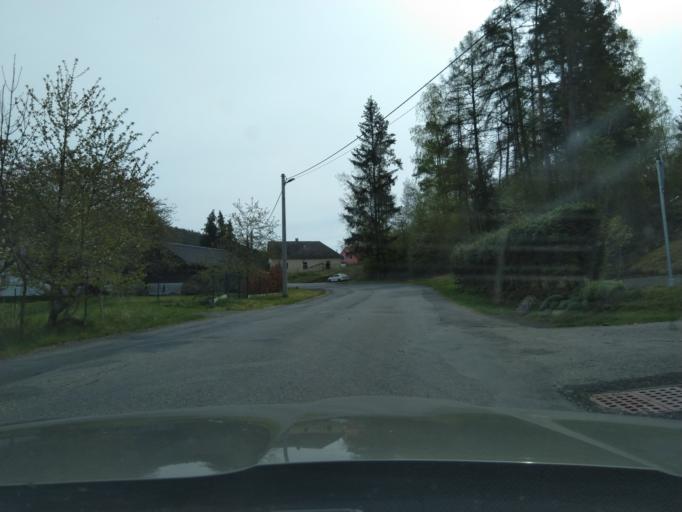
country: CZ
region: Plzensky
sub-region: Okres Klatovy
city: Susice
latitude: 49.2297
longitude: 13.5817
